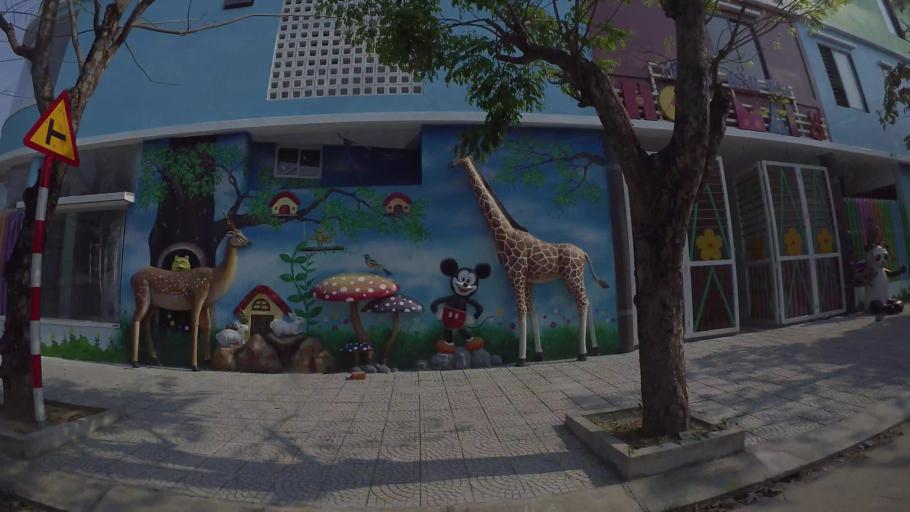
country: VN
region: Da Nang
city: Cam Le
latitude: 16.0158
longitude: 108.1985
